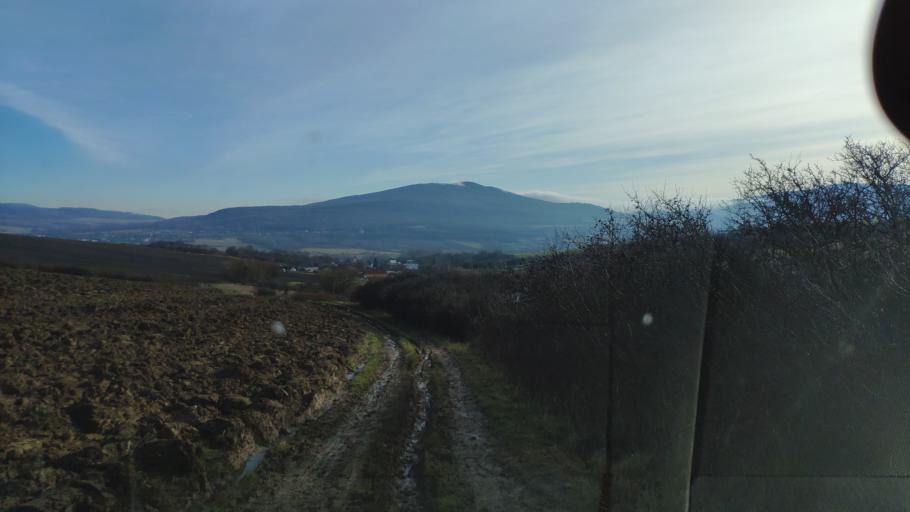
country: SK
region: Kosicky
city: Kosice
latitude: 48.6889
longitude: 21.3871
